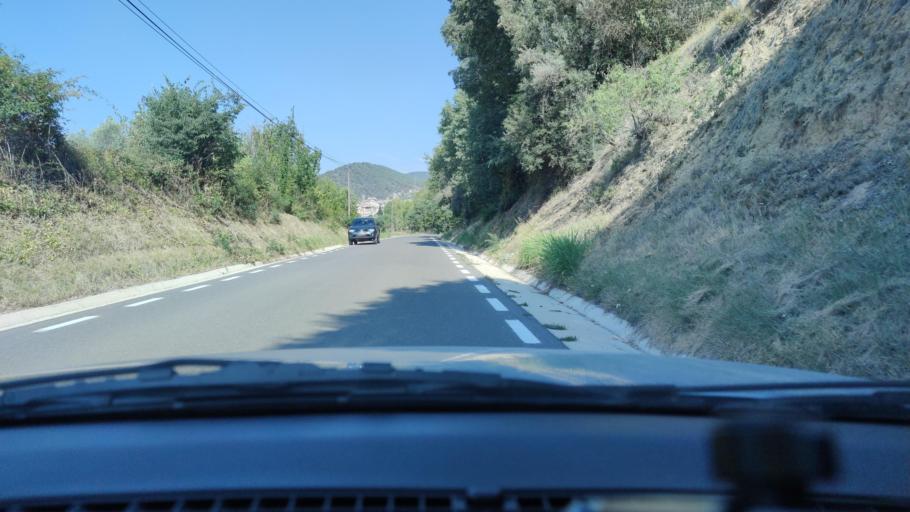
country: ES
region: Catalonia
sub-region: Provincia de Lleida
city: Tremp
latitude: 42.2109
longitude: 0.9430
